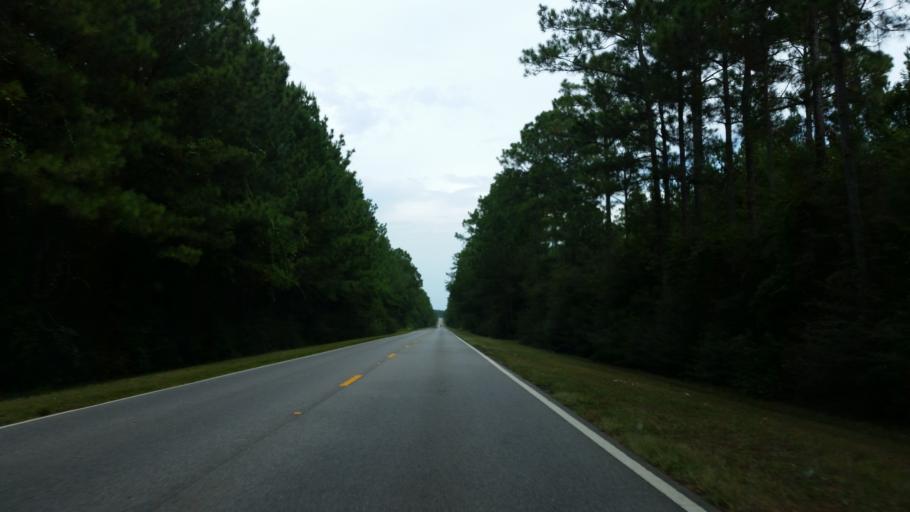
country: US
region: Florida
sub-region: Santa Rosa County
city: Wallace
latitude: 30.6730
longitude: -87.2428
